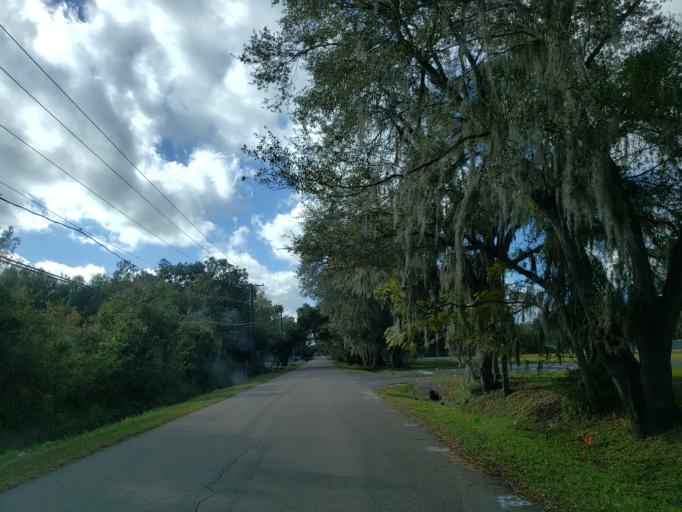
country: US
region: Florida
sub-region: Hillsborough County
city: Mango
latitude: 27.9668
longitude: -82.3308
